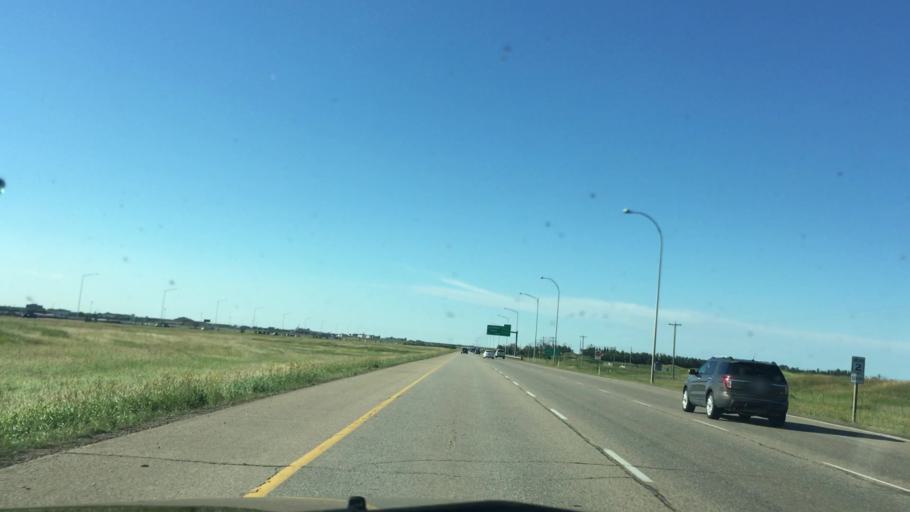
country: CA
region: Alberta
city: Leduc
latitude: 53.3325
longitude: -113.5498
